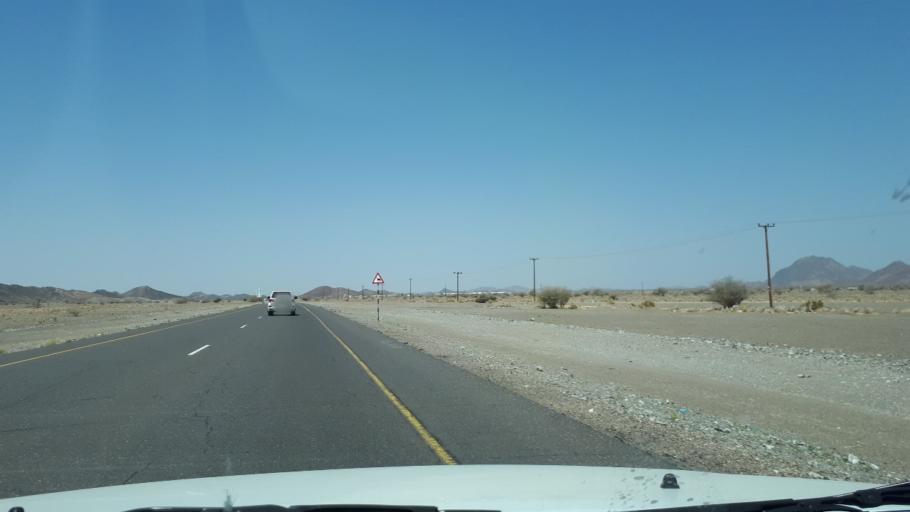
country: OM
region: Ash Sharqiyah
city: Ibra'
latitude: 22.6418
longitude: 58.4906
